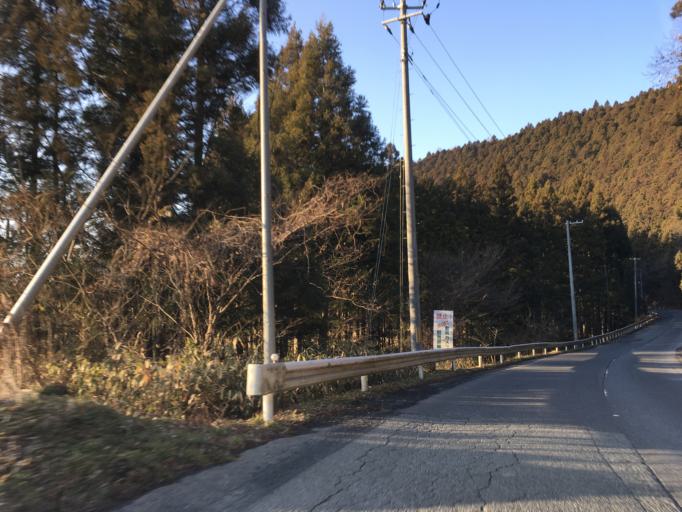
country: JP
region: Iwate
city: Ichinoseki
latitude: 38.8029
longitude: 141.2312
